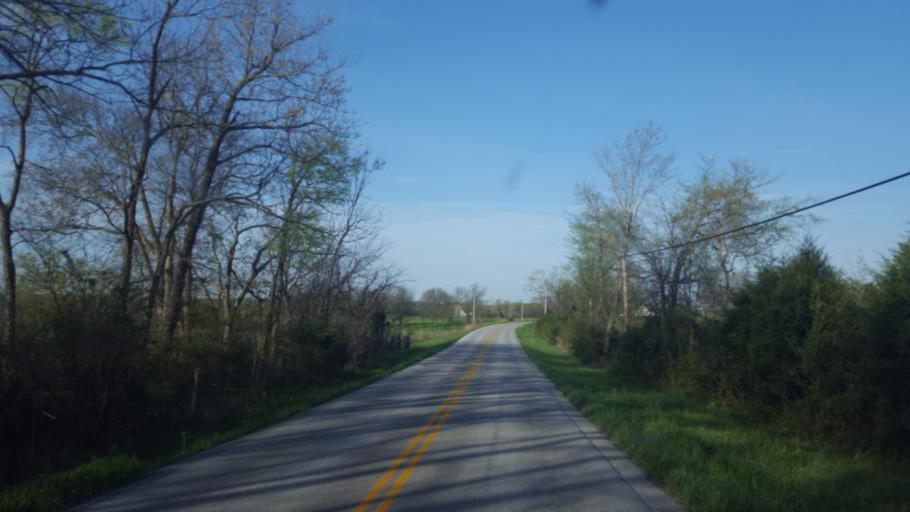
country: US
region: Kentucky
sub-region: Hardin County
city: Elizabethtown
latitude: 37.5001
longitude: -85.9419
